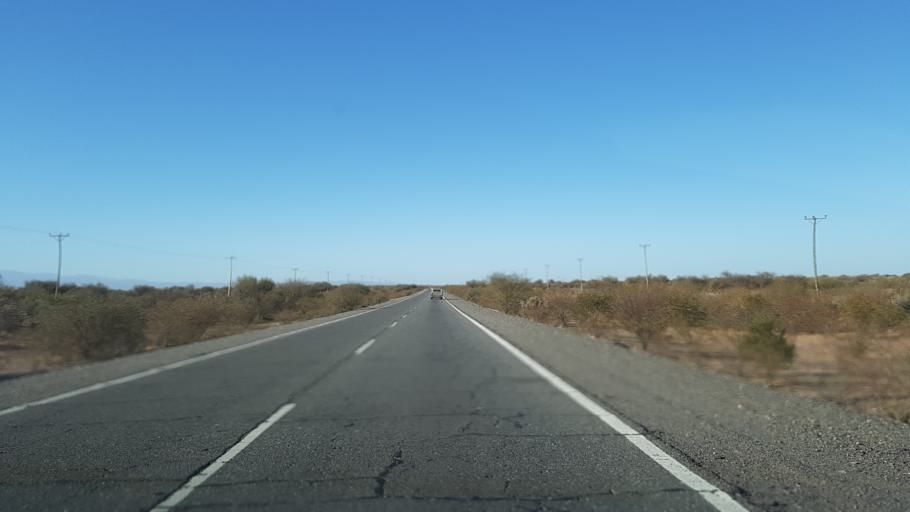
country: AR
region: San Juan
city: Caucete
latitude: -31.6035
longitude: -67.7071
